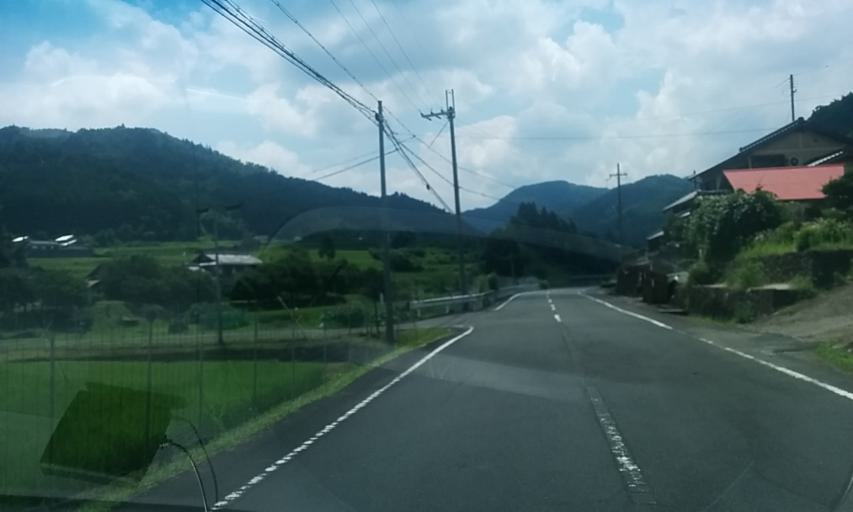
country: JP
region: Kyoto
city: Ayabe
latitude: 35.2003
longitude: 135.2221
